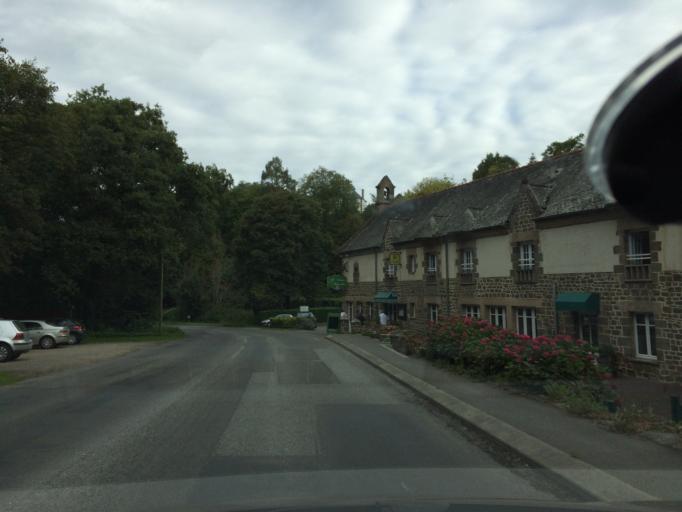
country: FR
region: Brittany
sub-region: Departement d'Ille-et-Vilaine
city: Hede-Bazouges
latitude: 48.2938
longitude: -1.8039
